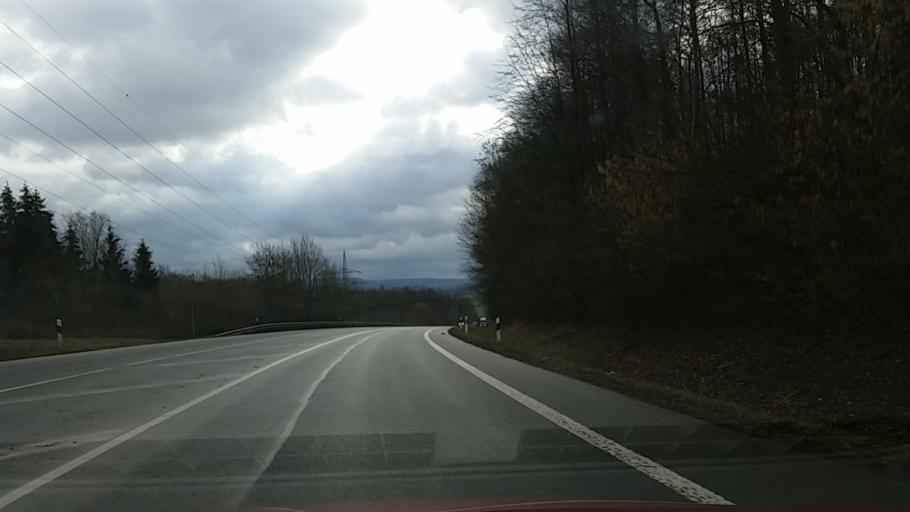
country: DE
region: Lower Saxony
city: Seesen
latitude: 51.8672
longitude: 10.1154
